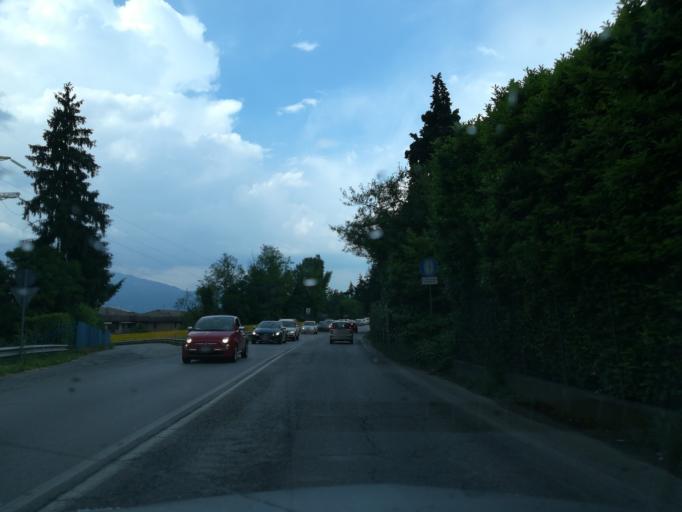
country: IT
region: Lombardy
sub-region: Provincia di Bergamo
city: Mozzo
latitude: 45.6943
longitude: 9.6029
